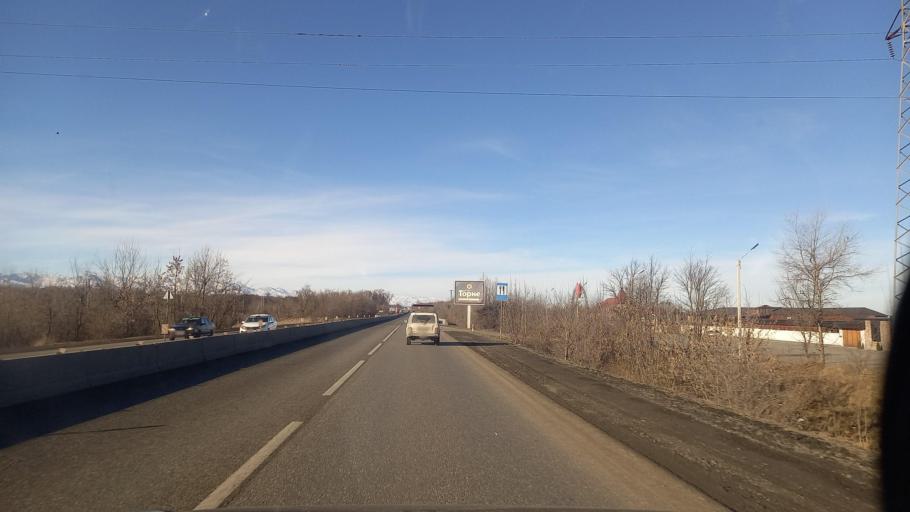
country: RU
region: North Ossetia
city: Gizel'
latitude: 43.0281
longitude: 44.5989
